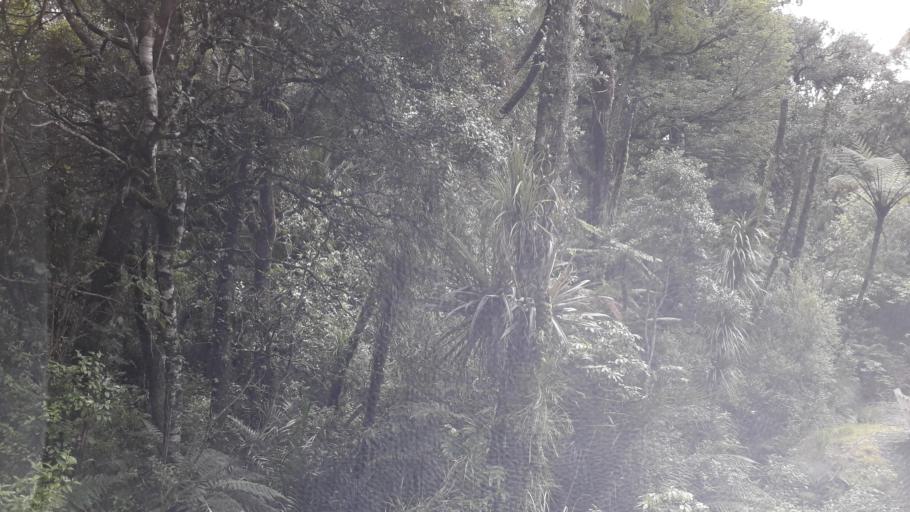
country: NZ
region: Northland
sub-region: Far North District
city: Kaitaia
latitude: -35.1926
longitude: 173.2825
